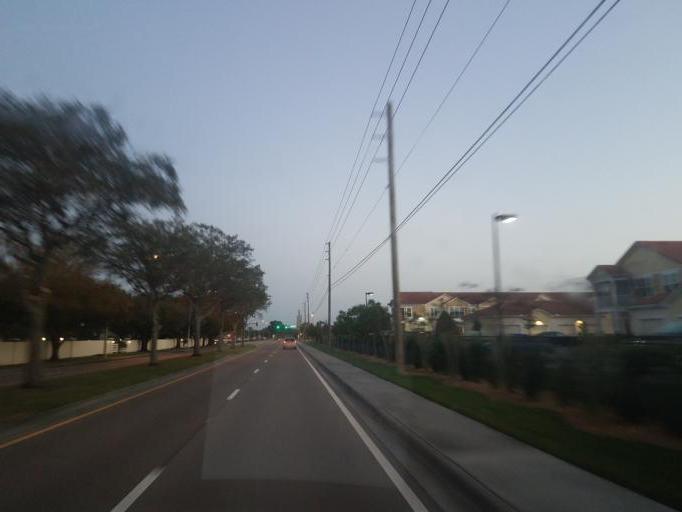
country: US
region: Florida
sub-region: Sarasota County
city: Lake Sarasota
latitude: 27.2872
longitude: -82.4521
